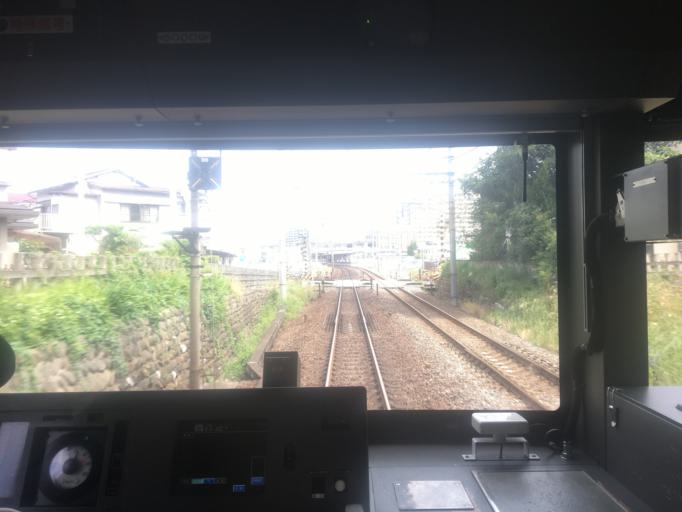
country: JP
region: Saitama
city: Sakado
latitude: 36.0324
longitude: 139.4021
